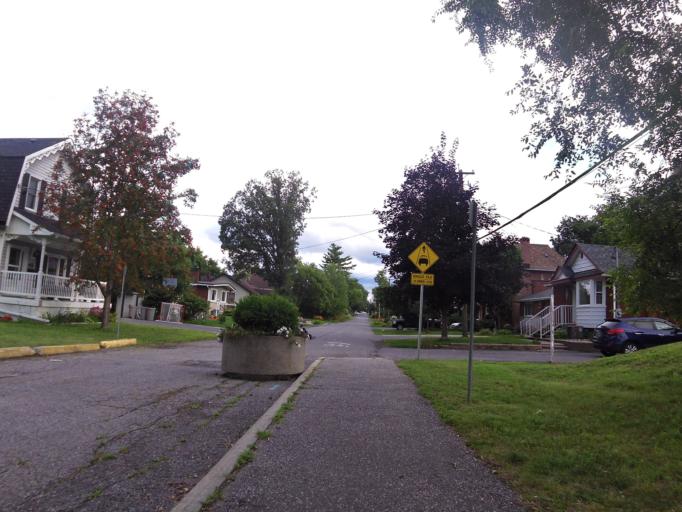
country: CA
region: Ontario
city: Bells Corners
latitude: 45.3704
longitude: -75.7814
